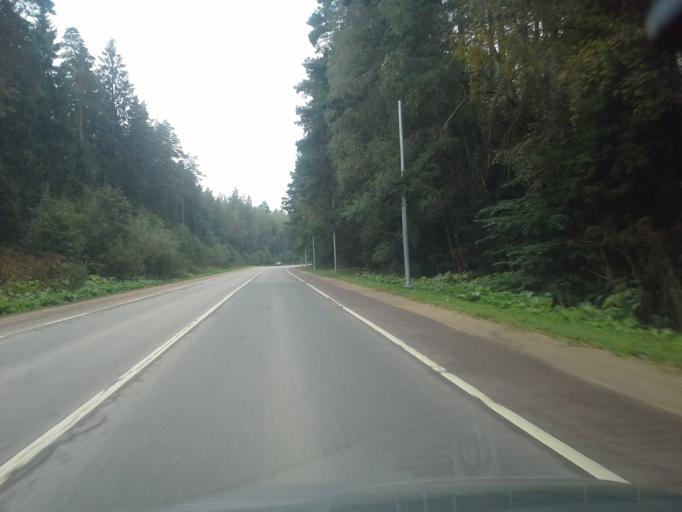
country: RU
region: Moskovskaya
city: Chupryakovo
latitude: 55.5683
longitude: 36.6193
